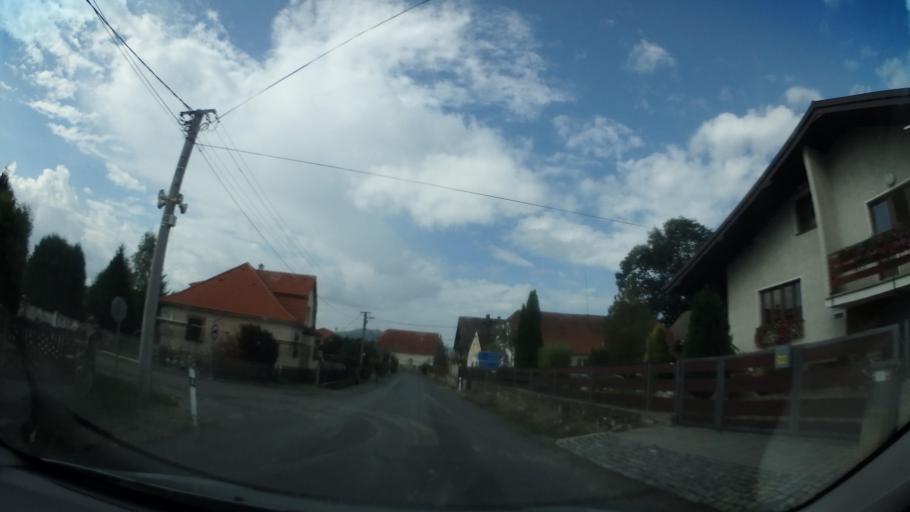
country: CZ
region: Plzensky
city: Horazd'ovice
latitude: 49.2670
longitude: 13.6330
